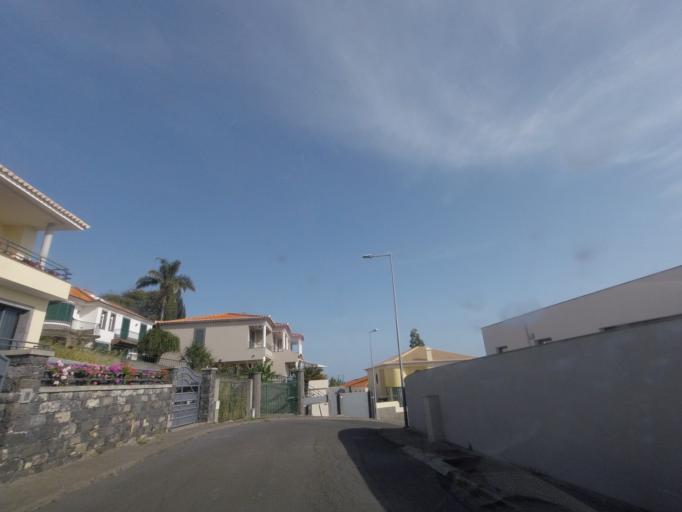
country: PT
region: Madeira
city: Camara de Lobos
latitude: 32.6397
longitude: -16.9413
